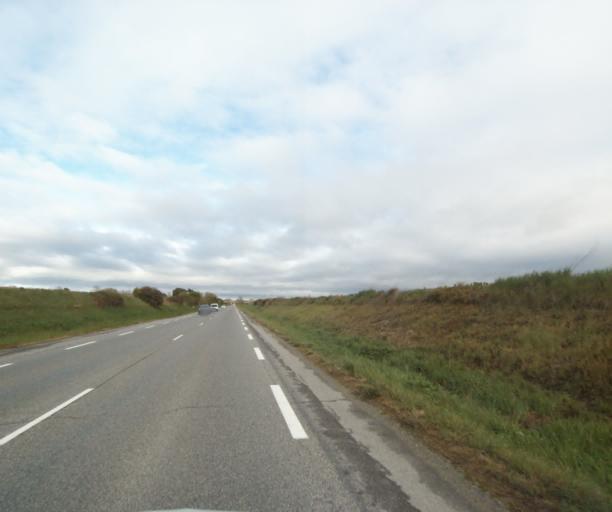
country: FR
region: Midi-Pyrenees
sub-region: Departement de l'Ariege
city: Saverdun
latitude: 43.2373
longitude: 1.5923
